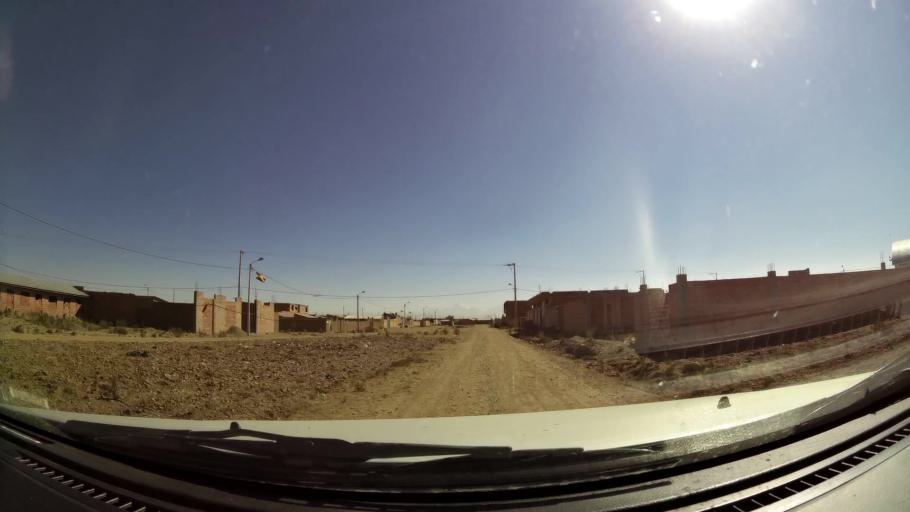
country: BO
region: La Paz
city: La Paz
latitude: -16.6241
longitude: -68.1953
